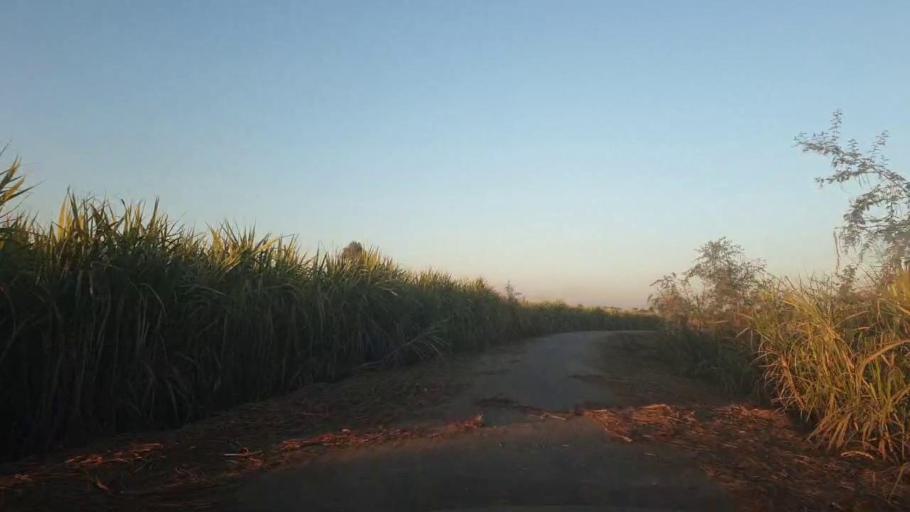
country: PK
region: Sindh
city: Ghotki
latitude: 28.0268
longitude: 69.2910
